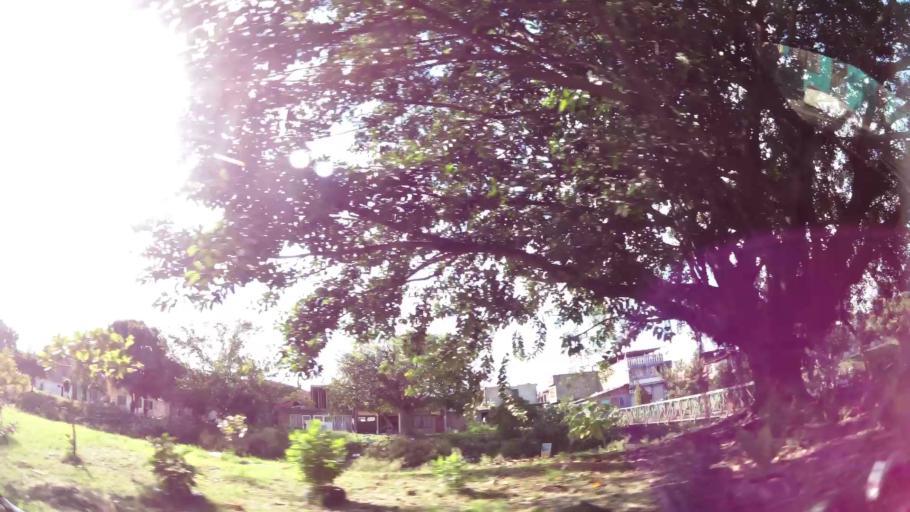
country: CO
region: Valle del Cauca
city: Cali
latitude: 3.4120
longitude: -76.4997
